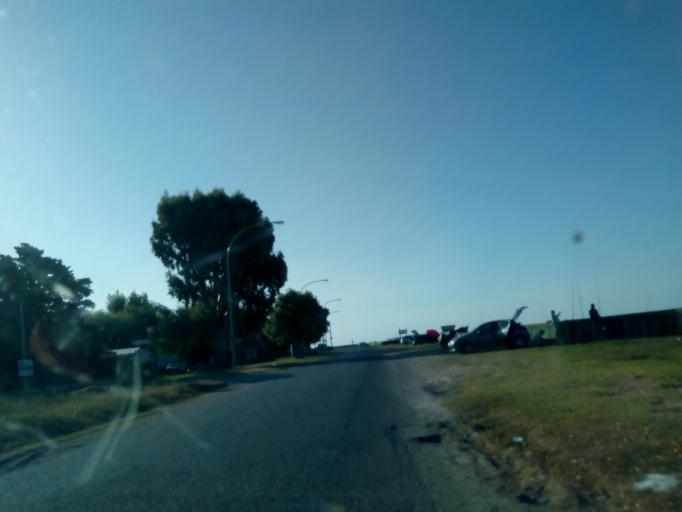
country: AR
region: Buenos Aires
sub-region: Partido de Ensenada
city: Ensenada
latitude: -34.7929
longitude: -57.9956
